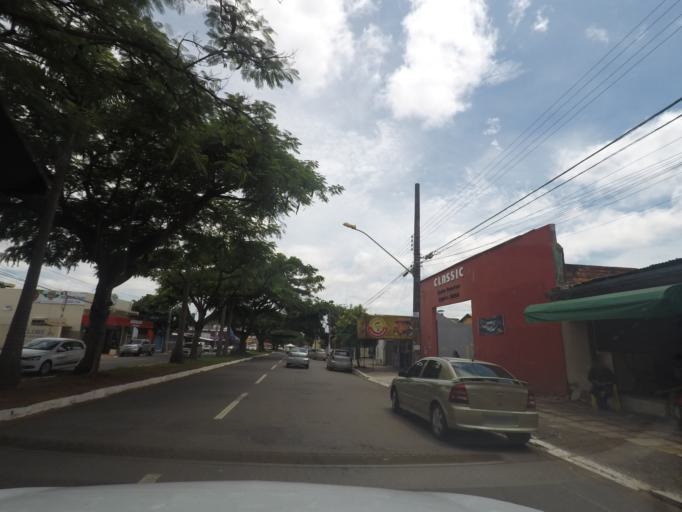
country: BR
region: Goias
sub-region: Goiania
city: Goiania
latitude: -16.6675
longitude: -49.2445
